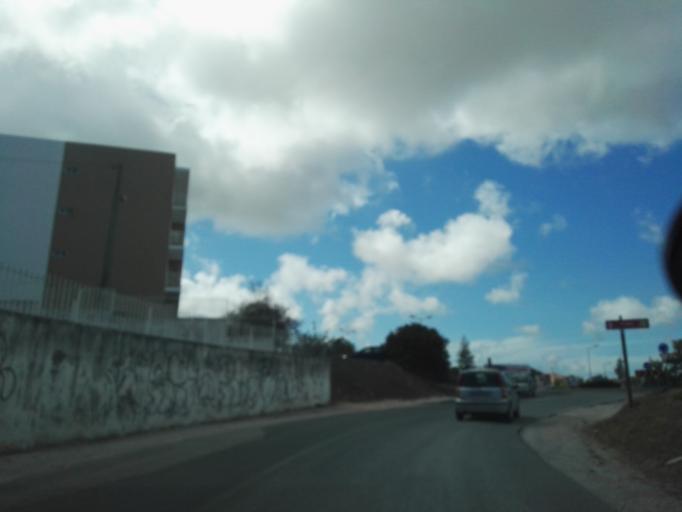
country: PT
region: Setubal
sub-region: Sesimbra
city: Sesimbra
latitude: 38.4648
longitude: -9.0965
